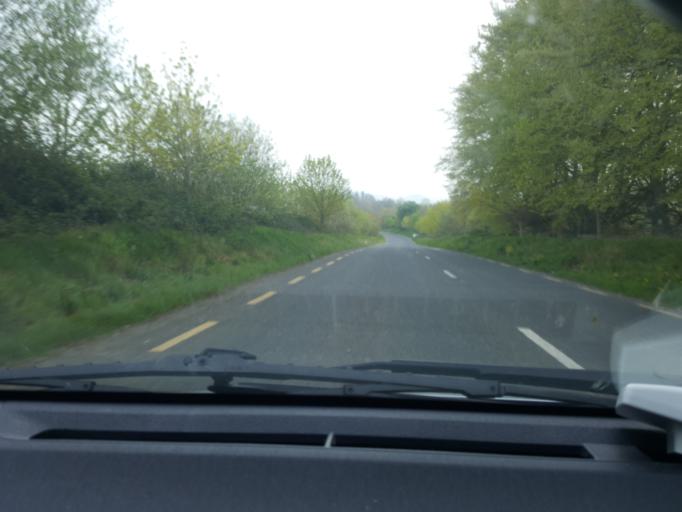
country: IE
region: Munster
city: Cahir
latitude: 52.3917
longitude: -7.9112
